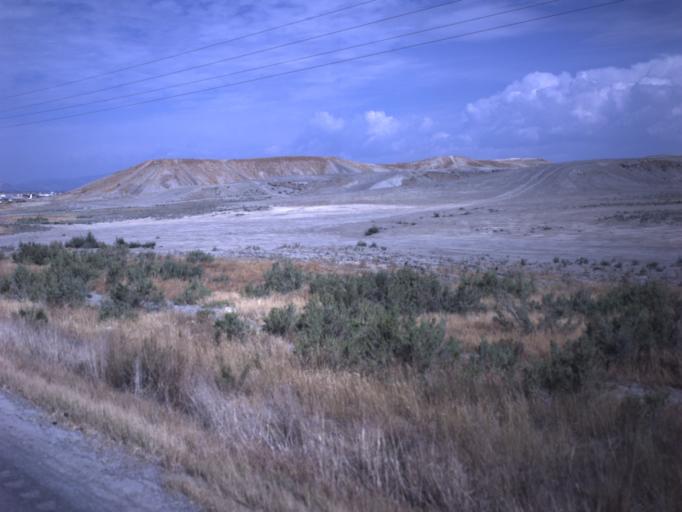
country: US
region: Utah
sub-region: Uintah County
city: Naples
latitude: 40.3694
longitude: -109.3916
